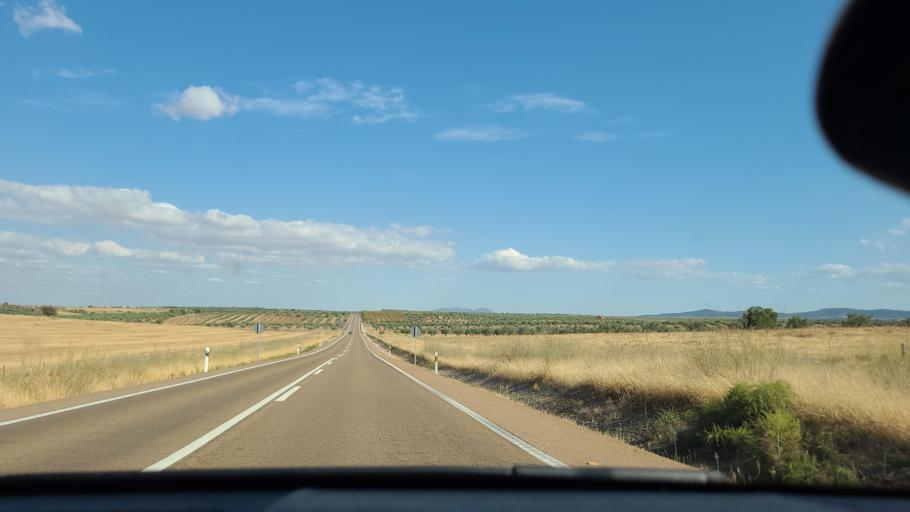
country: ES
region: Extremadura
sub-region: Provincia de Badajoz
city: Usagre
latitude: 38.3502
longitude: -6.1919
